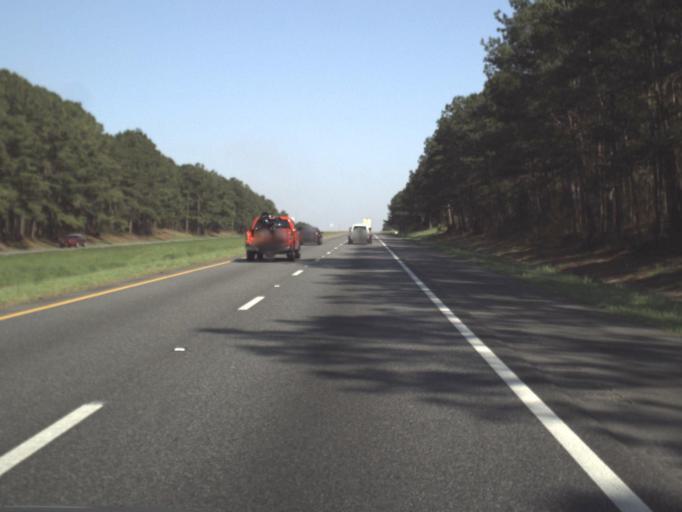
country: US
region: Florida
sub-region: Gadsden County
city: Quincy
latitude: 30.5305
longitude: -84.5525
